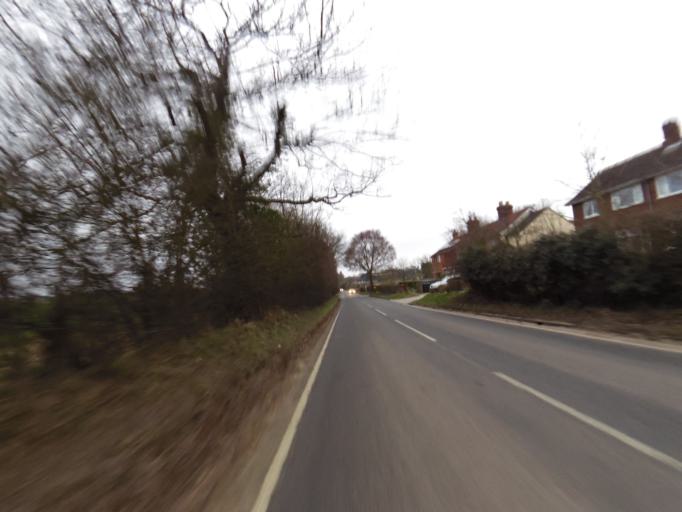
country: GB
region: England
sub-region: Suffolk
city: Ipswich
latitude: 52.0939
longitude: 1.1553
